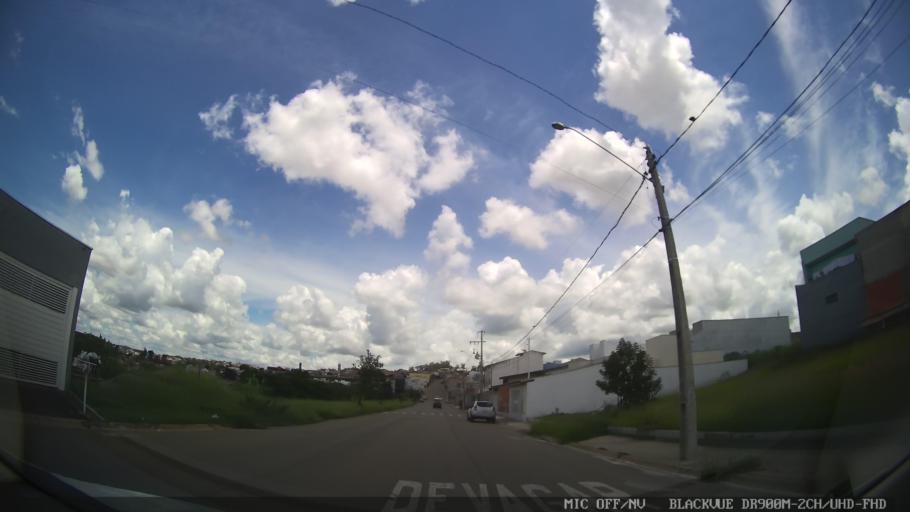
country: BR
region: Sao Paulo
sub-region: Braganca Paulista
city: Braganca Paulista
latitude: -22.9302
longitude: -46.5664
